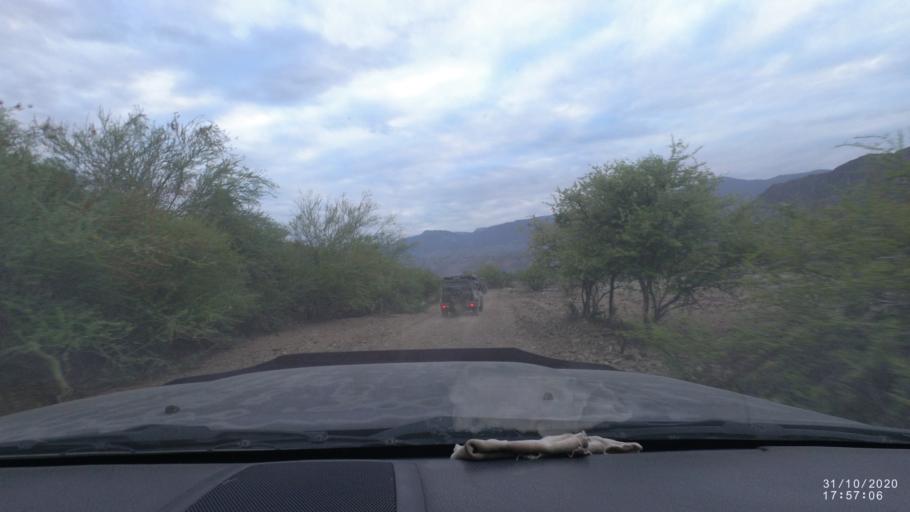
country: BO
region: Chuquisaca
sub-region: Provincia Zudanez
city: Mojocoya
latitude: -18.6490
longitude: -64.5316
